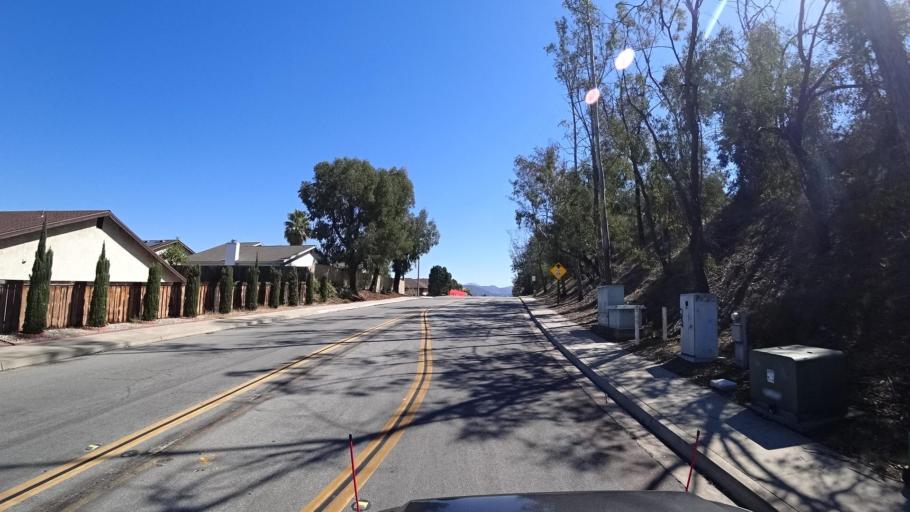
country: US
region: California
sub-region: San Diego County
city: Rancho San Diego
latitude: 32.7510
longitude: -116.9202
